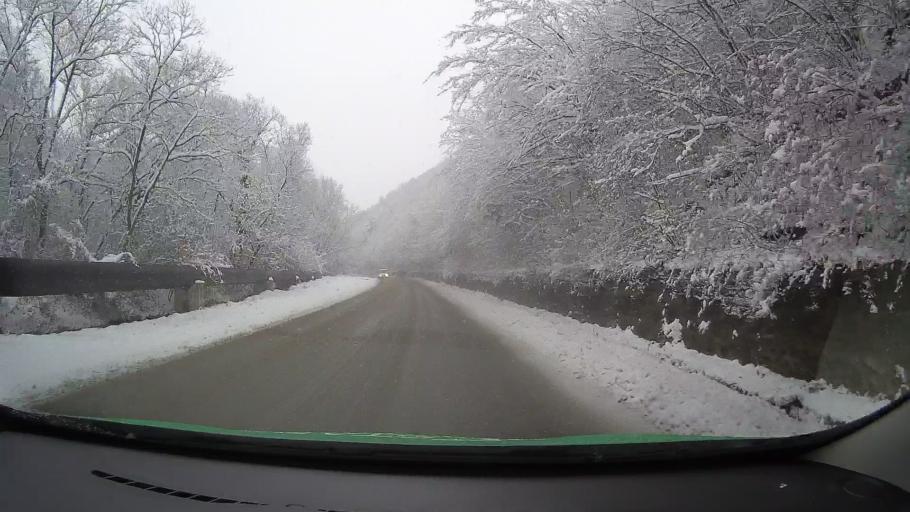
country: RO
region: Hunedoara
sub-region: Comuna Teliucu Inferior
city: Teliucu Inferior
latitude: 45.7250
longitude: 22.8789
